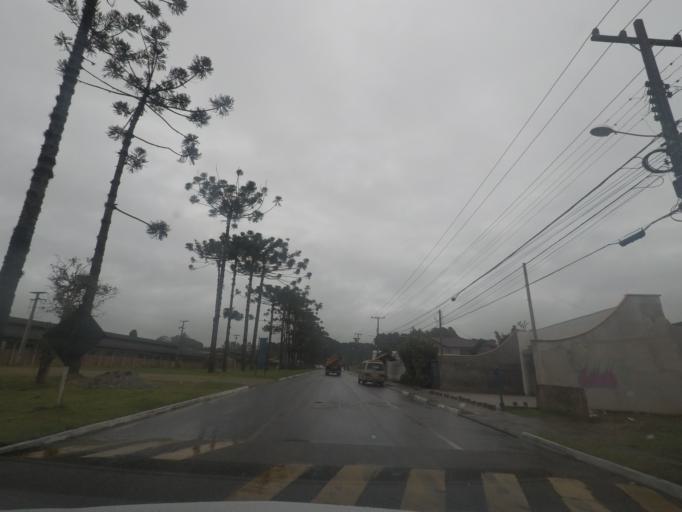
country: BR
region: Parana
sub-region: Quatro Barras
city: Quatro Barras
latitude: -25.3792
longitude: -49.1218
